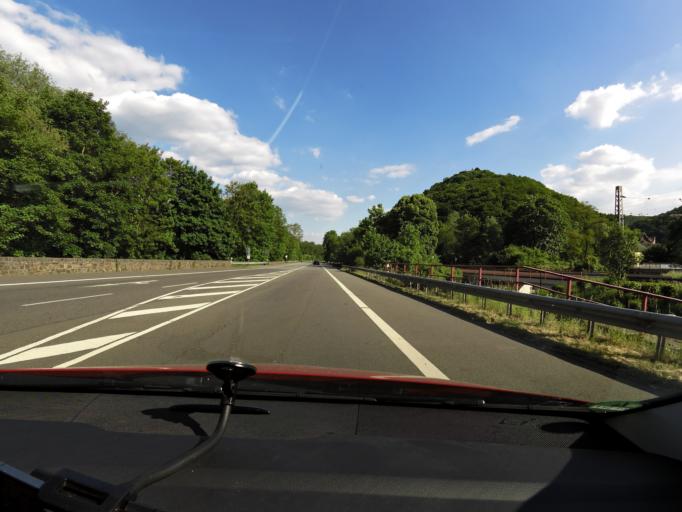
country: DE
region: Rheinland-Pfalz
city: Bad Honningen
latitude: 50.5010
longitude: 7.3103
